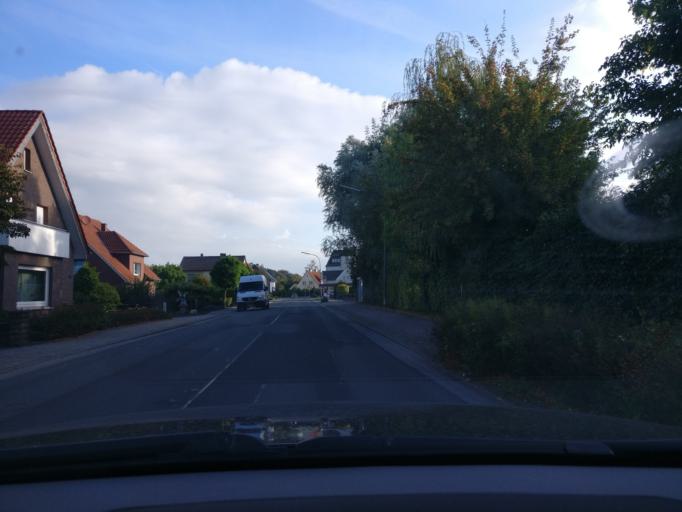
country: DE
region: Lower Saxony
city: Melle
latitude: 52.1865
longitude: 8.3372
